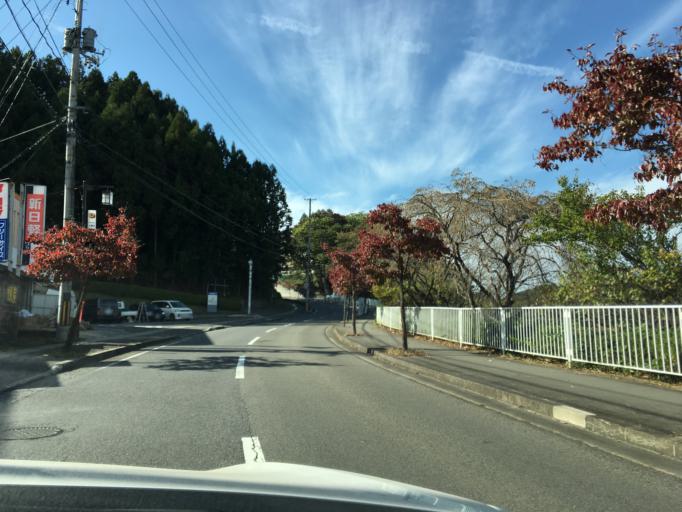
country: JP
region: Fukushima
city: Miharu
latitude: 37.4469
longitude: 140.4854
